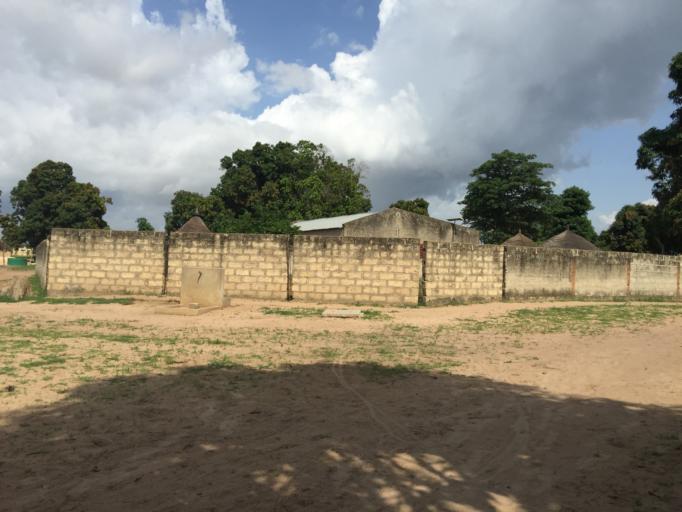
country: SN
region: Fatick
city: Sokone
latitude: 13.7555
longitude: -16.4284
